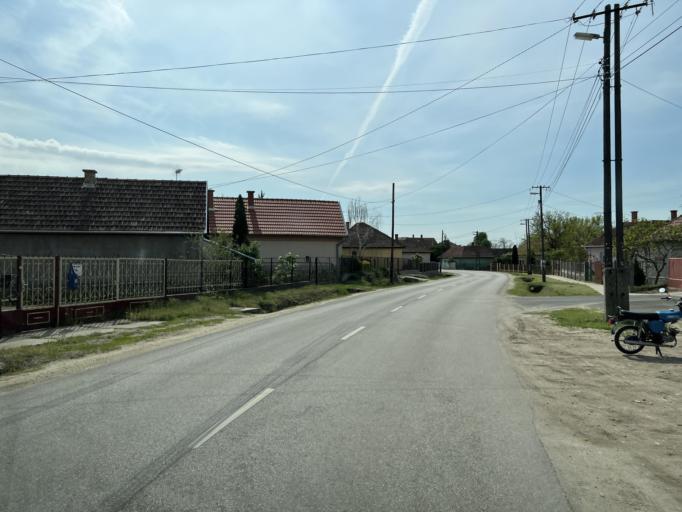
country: HU
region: Pest
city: Tapioszolos
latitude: 47.2960
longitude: 19.8339
